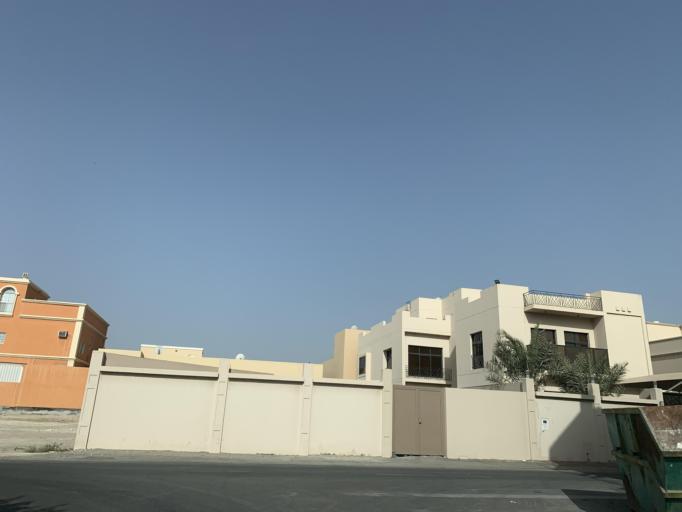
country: BH
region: Northern
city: Ar Rifa'
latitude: 26.1436
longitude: 50.5815
